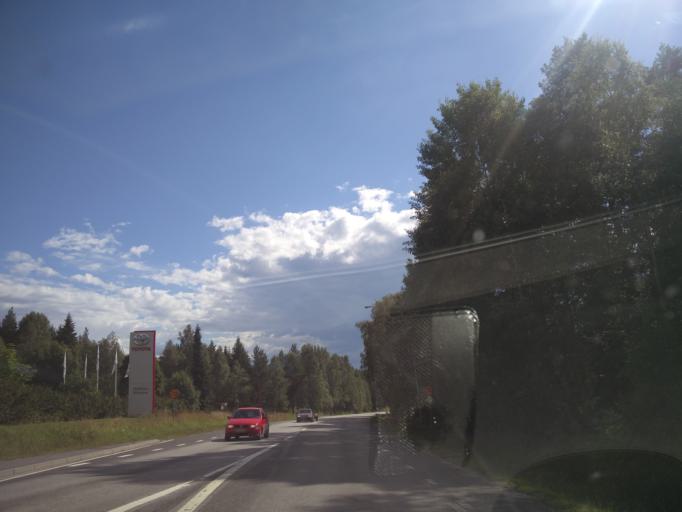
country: SE
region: OErebro
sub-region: Hallefors Kommun
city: Haellefors
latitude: 59.7697
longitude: 14.5231
